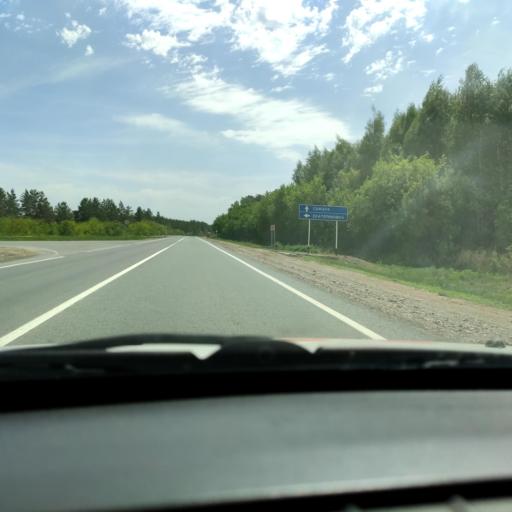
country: RU
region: Samara
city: Mirnyy
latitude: 53.5683
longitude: 50.2915
